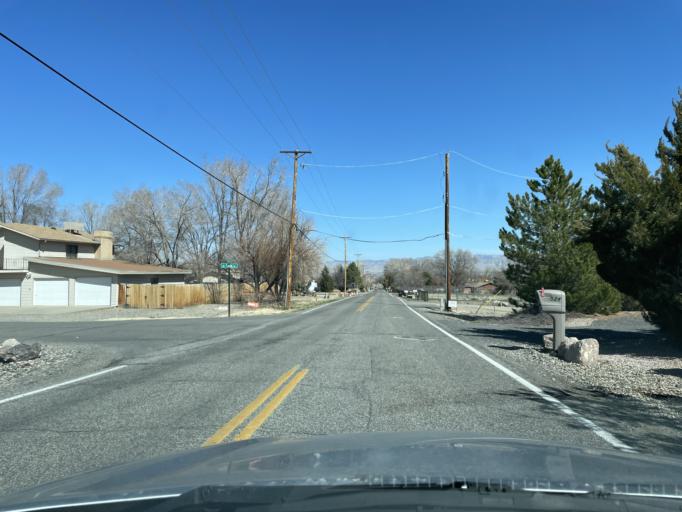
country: US
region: Colorado
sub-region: Mesa County
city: Redlands
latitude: 39.0811
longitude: -108.6688
